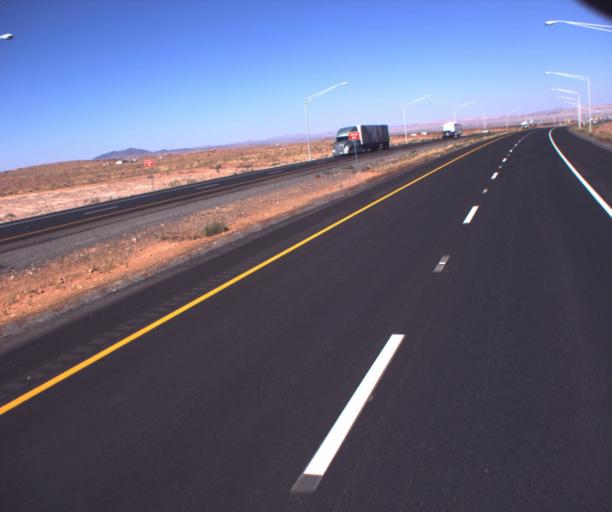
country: US
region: Arizona
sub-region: Coconino County
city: Tuba City
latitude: 35.8445
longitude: -111.4334
